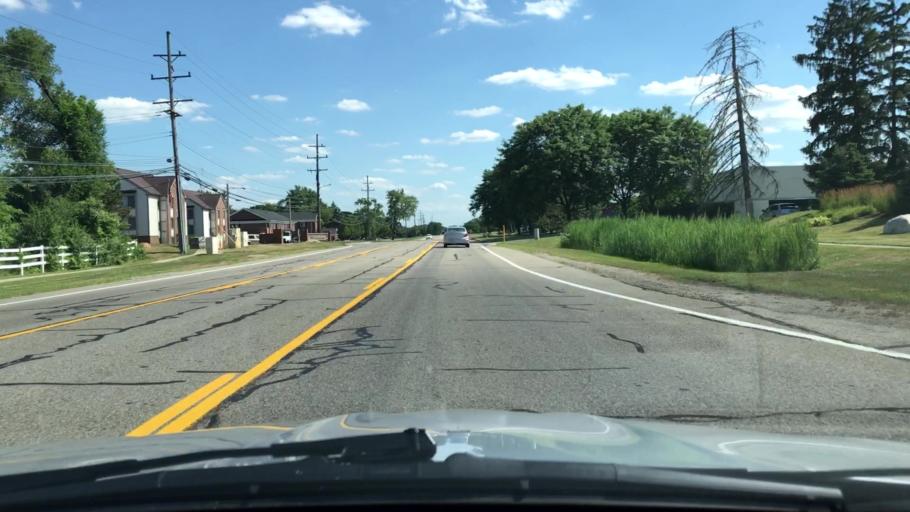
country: US
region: Michigan
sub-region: Oakland County
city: Farmington Hills
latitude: 42.4764
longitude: -83.4162
